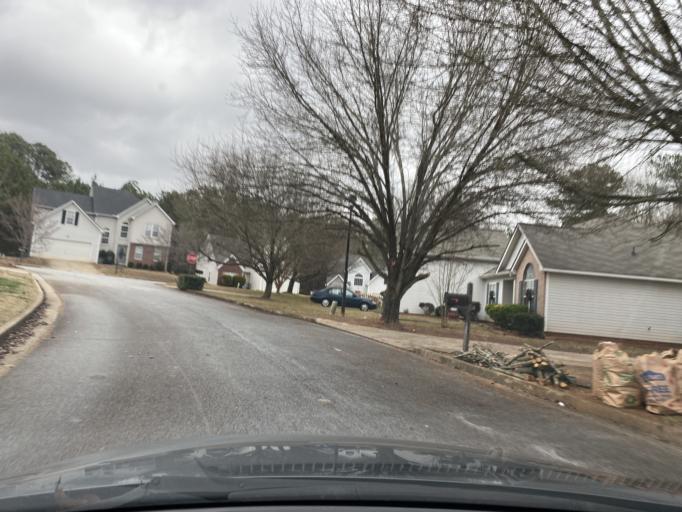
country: US
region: Georgia
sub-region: DeKalb County
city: Pine Mountain
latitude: 33.6972
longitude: -84.1640
